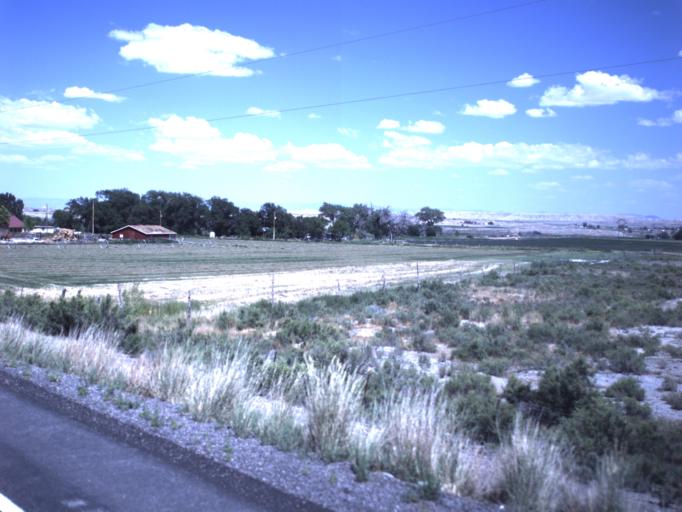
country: US
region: Utah
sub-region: Emery County
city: Huntington
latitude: 39.2932
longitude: -110.9676
